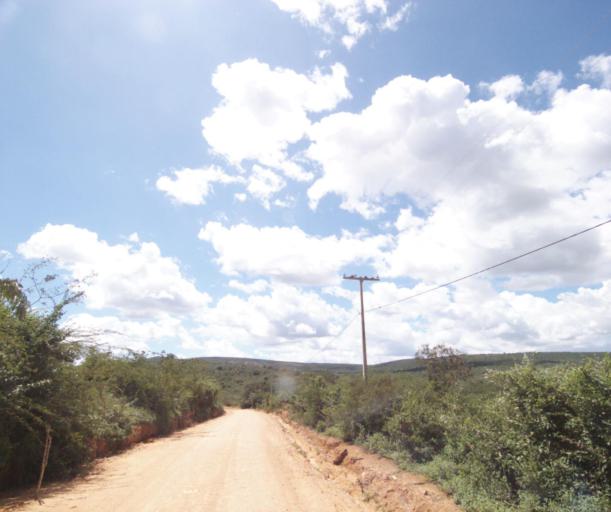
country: BR
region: Bahia
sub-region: Pocoes
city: Pocoes
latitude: -14.2973
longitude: -40.6373
